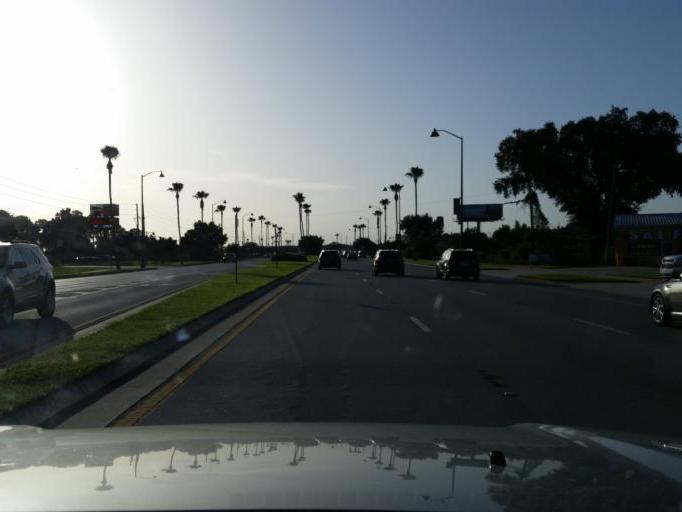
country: US
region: Florida
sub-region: Polk County
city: Citrus Ridge
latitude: 28.3428
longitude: -81.6000
